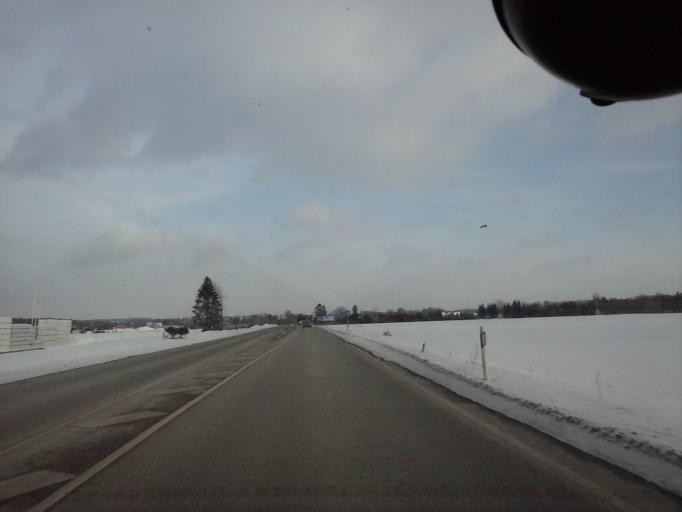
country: EE
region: Tartu
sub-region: Noo vald
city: Noo
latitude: 58.3541
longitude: 26.5916
